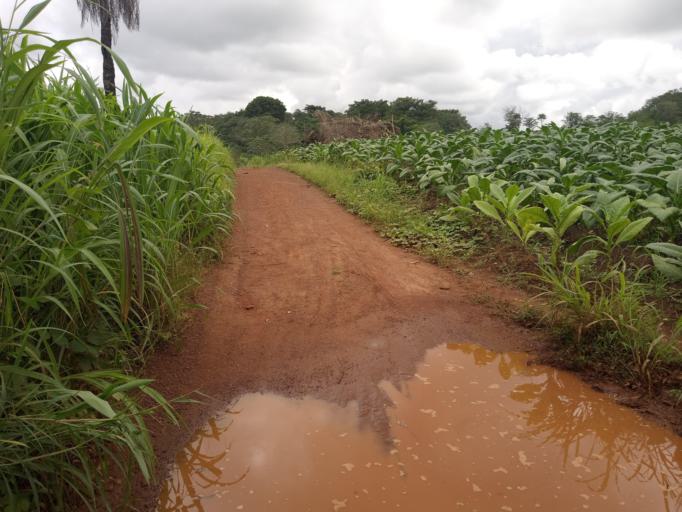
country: SL
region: Northern Province
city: Kamakwie
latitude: 9.4801
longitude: -12.2478
